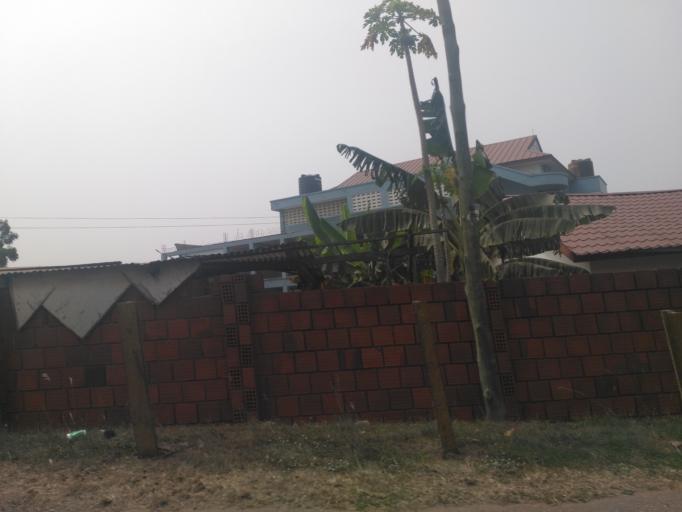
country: GH
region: Ashanti
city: Kumasi
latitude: 6.6888
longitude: -1.6328
